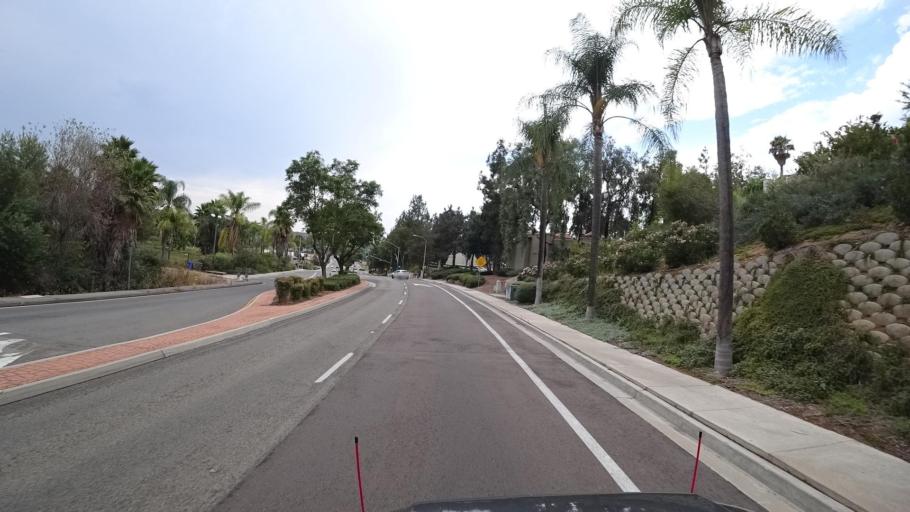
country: US
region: California
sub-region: San Diego County
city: Escondido
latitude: 33.1372
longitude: -117.1183
